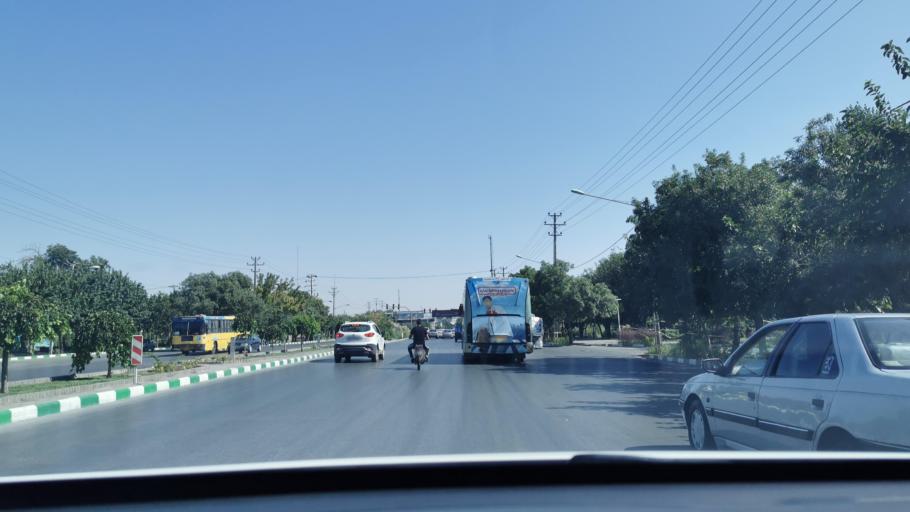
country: IR
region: Razavi Khorasan
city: Mashhad
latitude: 36.3334
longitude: 59.6254
